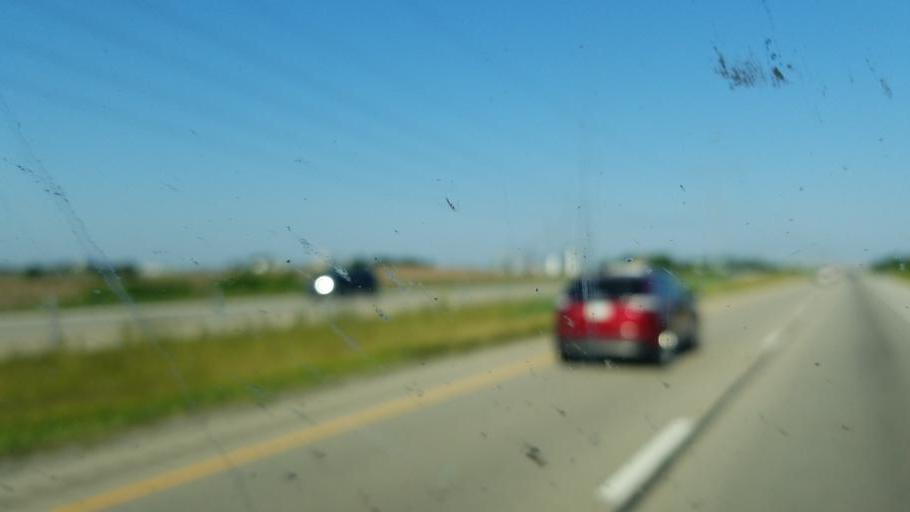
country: US
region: Illinois
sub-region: LaSalle County
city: Seneca
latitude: 41.3764
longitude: -88.6060
